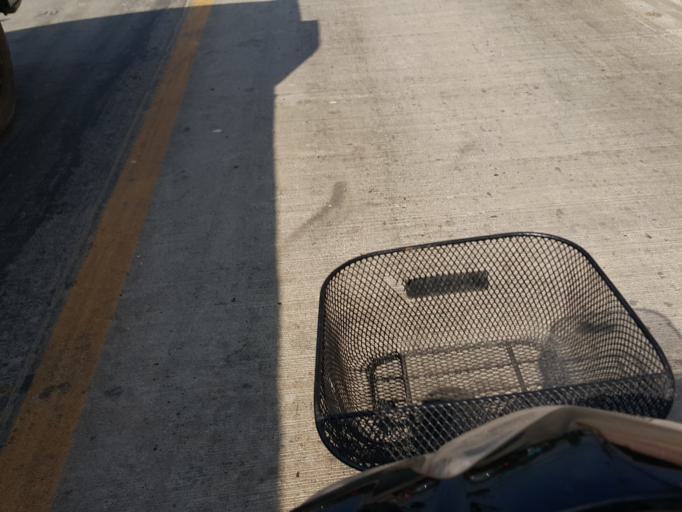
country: TH
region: Lamphun
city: Ban Thi
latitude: 18.6339
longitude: 99.0514
